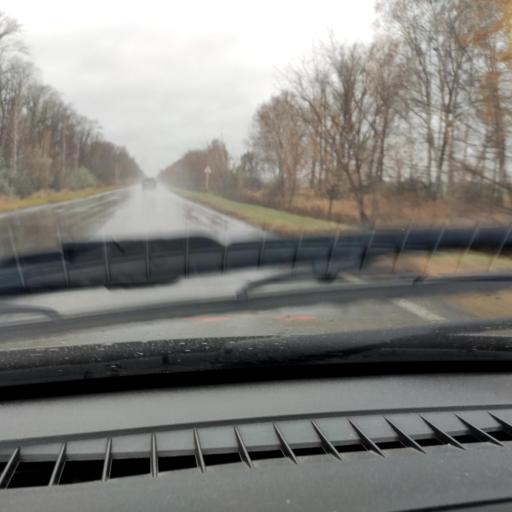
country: RU
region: Samara
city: Tol'yatti
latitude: 53.6748
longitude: 49.2686
